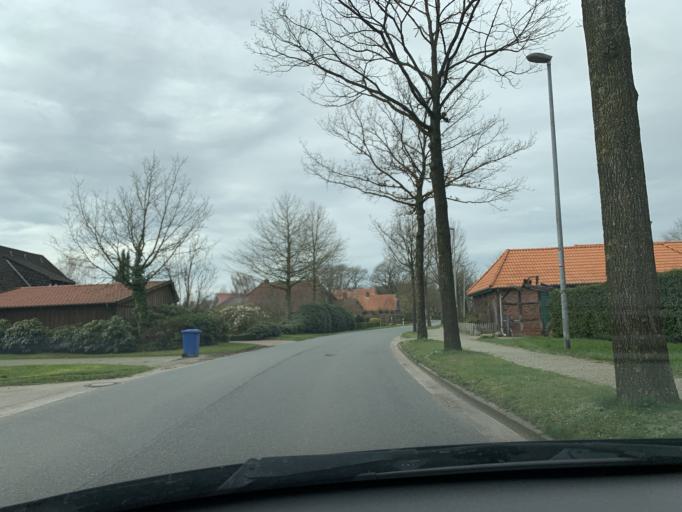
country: DE
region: Lower Saxony
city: Bad Zwischenahn
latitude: 53.1584
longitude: 7.9826
